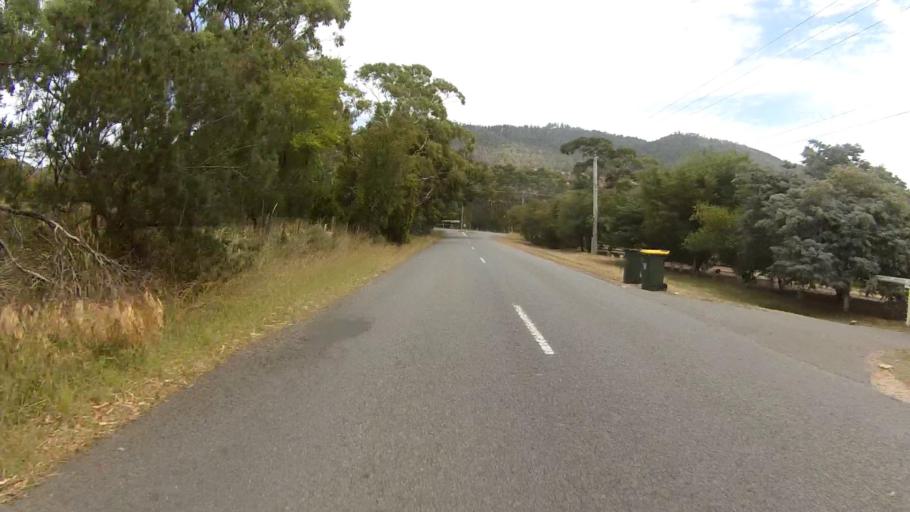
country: AU
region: Tasmania
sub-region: Clarence
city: Acton Park
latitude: -42.8679
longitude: 147.4855
